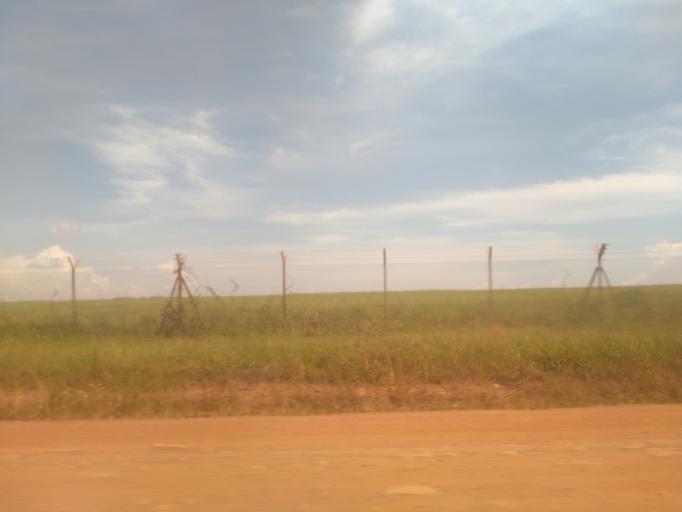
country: UG
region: Central Region
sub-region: Wakiso District
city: Entebbe
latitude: 0.0501
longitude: 32.4355
